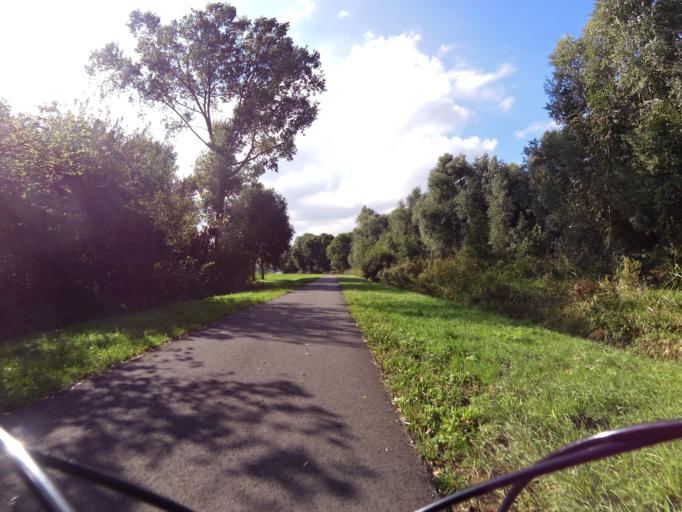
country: NL
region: South Holland
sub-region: Gemeente Voorschoten
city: Voorschoten
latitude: 52.1113
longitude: 4.4591
